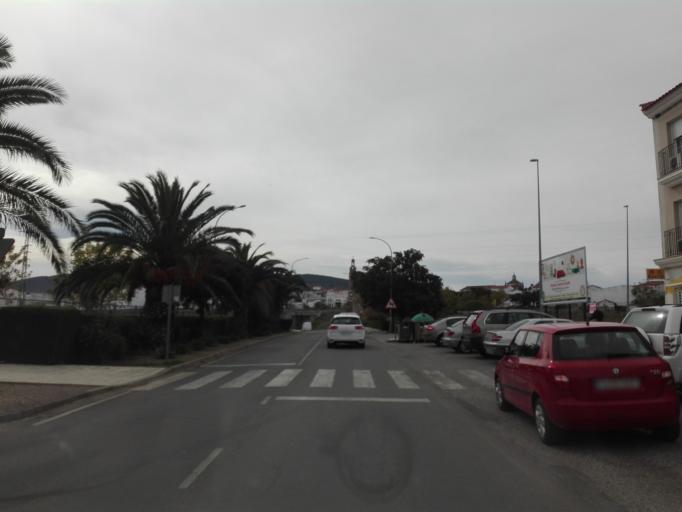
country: ES
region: Extremadura
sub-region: Provincia de Badajoz
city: Llerena
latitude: 38.2430
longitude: -6.0144
